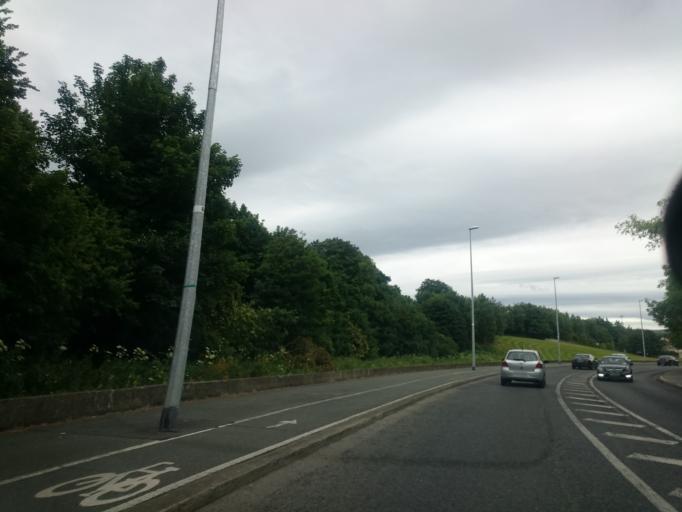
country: IE
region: Leinster
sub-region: South Dublin
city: Terenure
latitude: 53.3016
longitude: -6.2862
